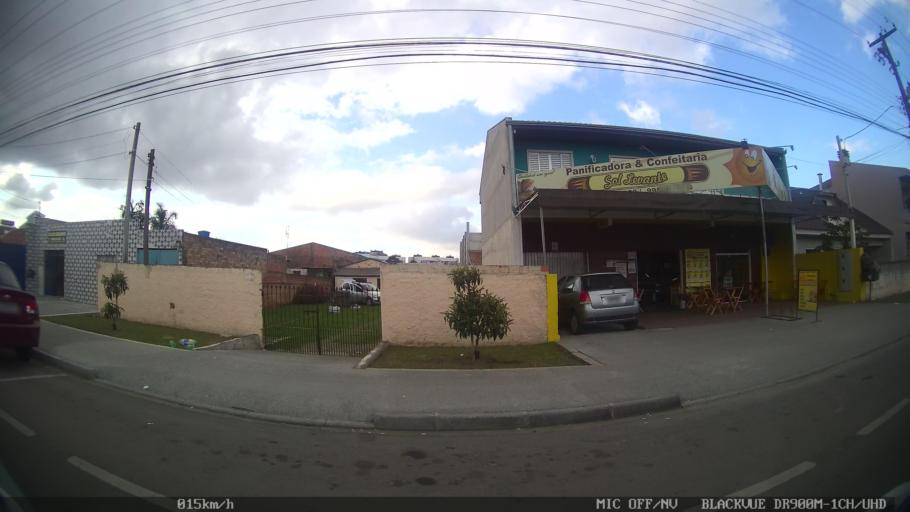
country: BR
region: Parana
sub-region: Pinhais
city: Pinhais
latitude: -25.4371
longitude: -49.1992
